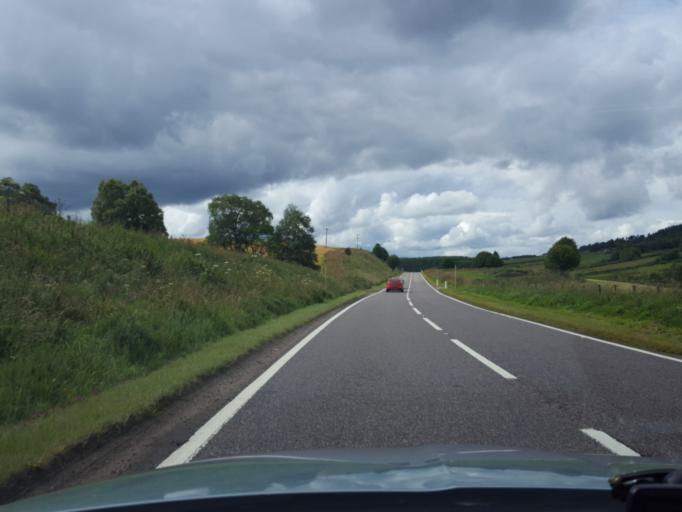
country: GB
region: Scotland
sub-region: Moray
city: Rothes
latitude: 57.4411
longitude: -3.2871
